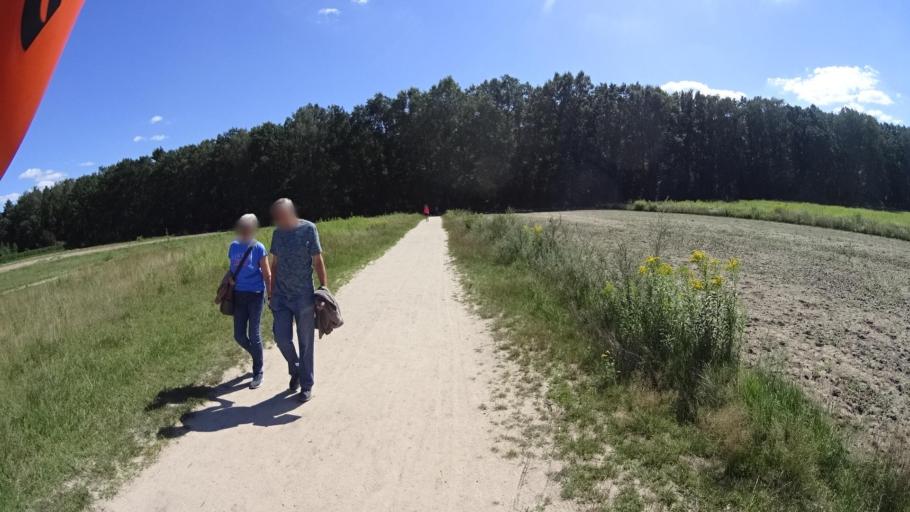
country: PL
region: Masovian Voivodeship
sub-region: Warszawa
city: Kabaty
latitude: 52.1250
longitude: 21.0761
